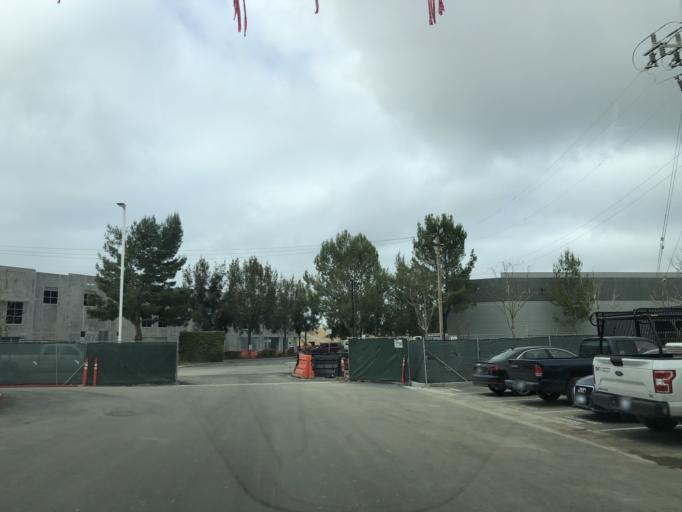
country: US
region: California
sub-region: Alameda County
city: Newark
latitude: 37.5211
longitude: -122.0318
